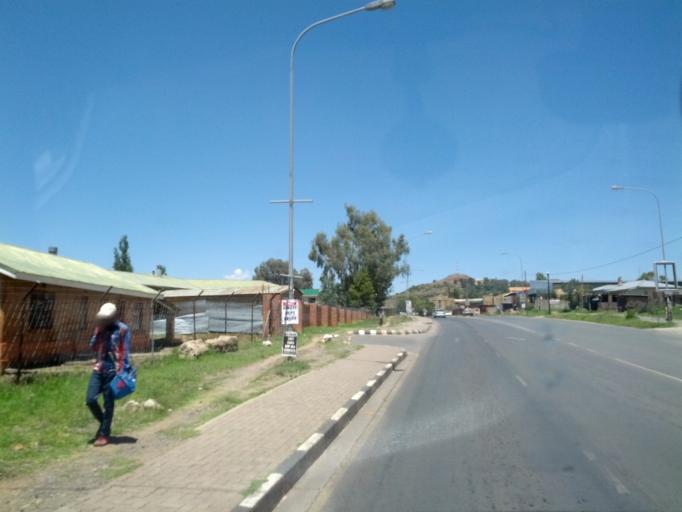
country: LS
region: Maseru
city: Maseru
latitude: -29.3056
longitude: 27.4840
